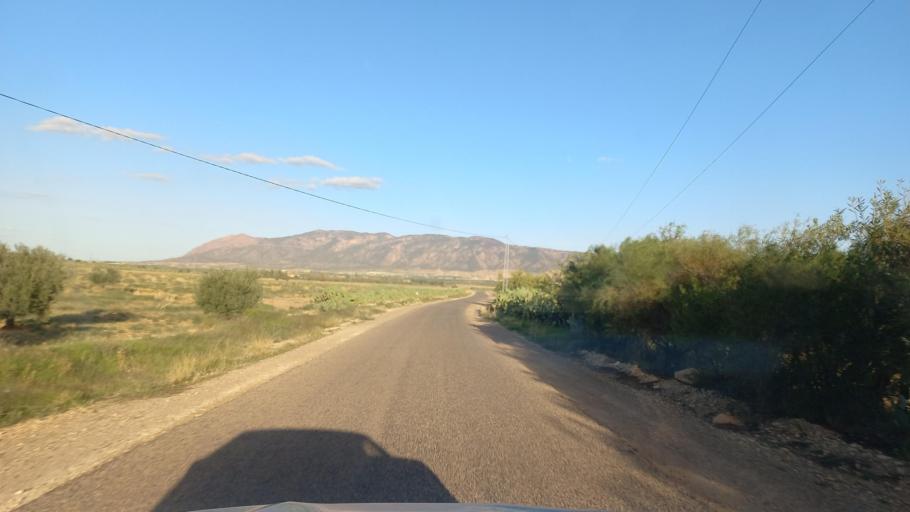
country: TN
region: Al Qasrayn
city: Sbiba
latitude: 35.4111
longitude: 9.1346
